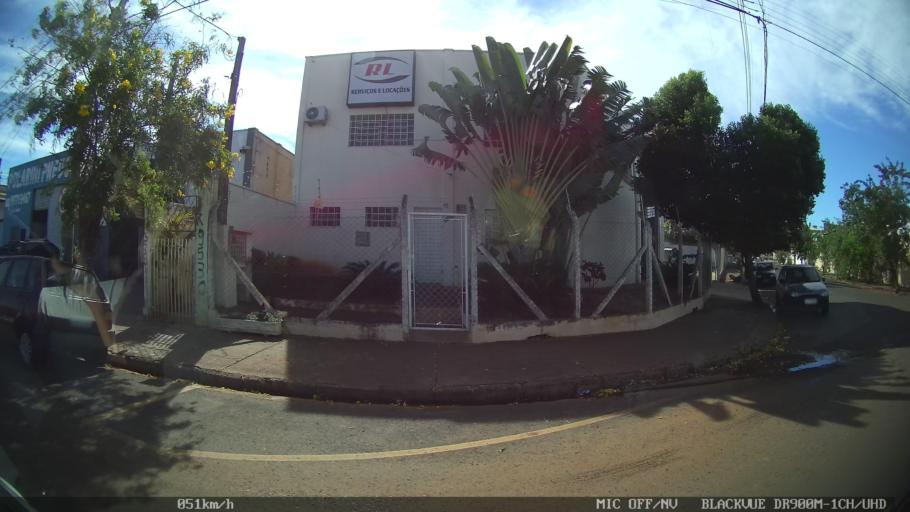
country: BR
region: Sao Paulo
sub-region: Sao Jose Do Rio Preto
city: Sao Jose do Rio Preto
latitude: -20.8502
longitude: -49.3843
